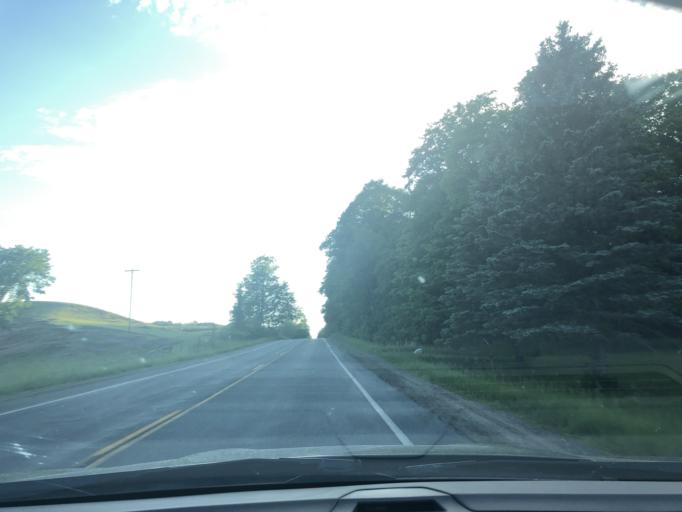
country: US
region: Michigan
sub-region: Missaukee County
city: Lake City
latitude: 44.4668
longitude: -85.0988
